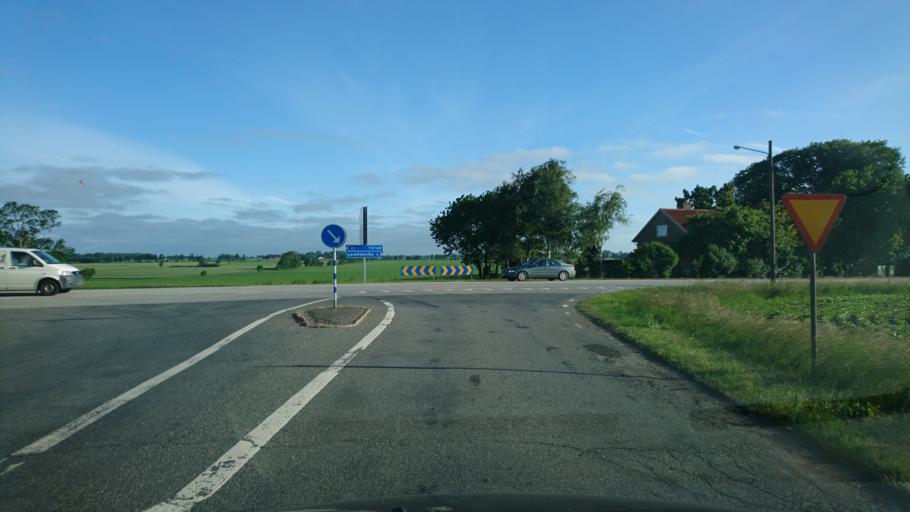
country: SE
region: Skane
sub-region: Tomelilla Kommun
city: Tomelilla
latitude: 55.4909
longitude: 14.1016
